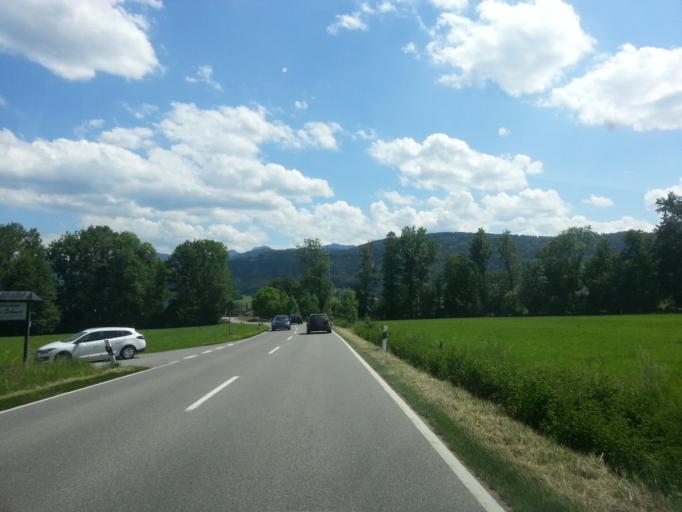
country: DE
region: Bavaria
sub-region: Upper Bavaria
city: Bad Feilnbach
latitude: 47.8056
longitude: 11.9651
